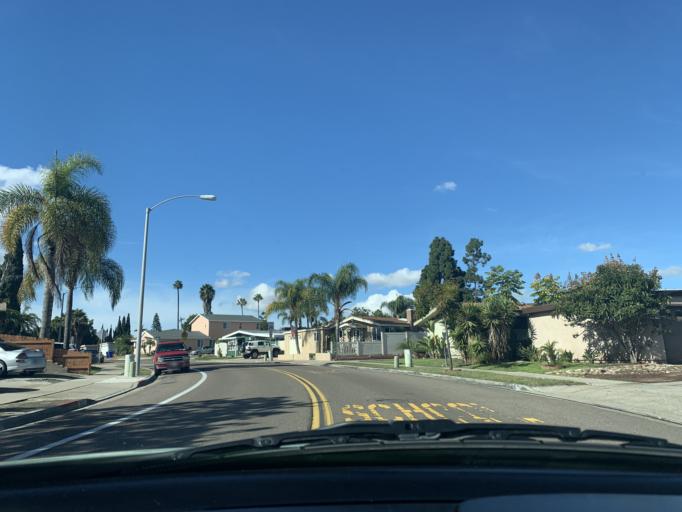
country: US
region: California
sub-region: San Diego County
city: San Diego
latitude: 32.8043
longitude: -117.1357
